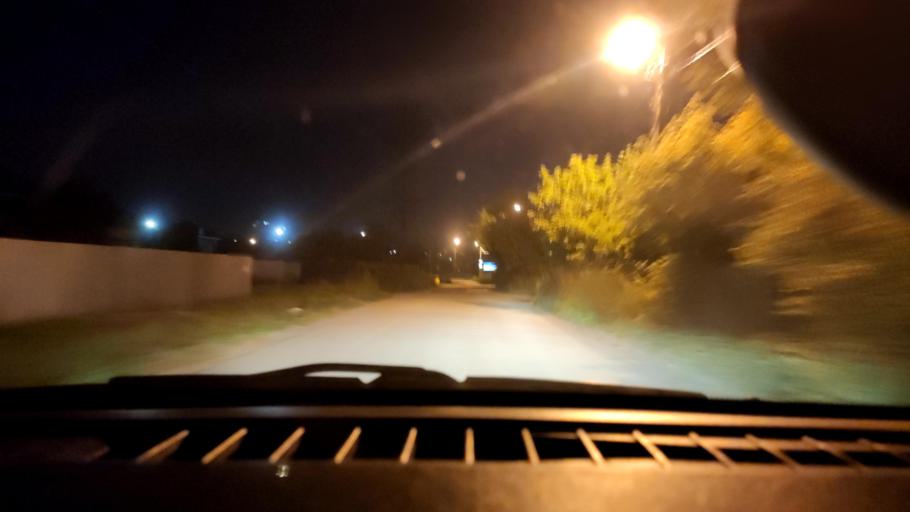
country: RU
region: Samara
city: Novokuybyshevsk
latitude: 53.0914
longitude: 50.0007
